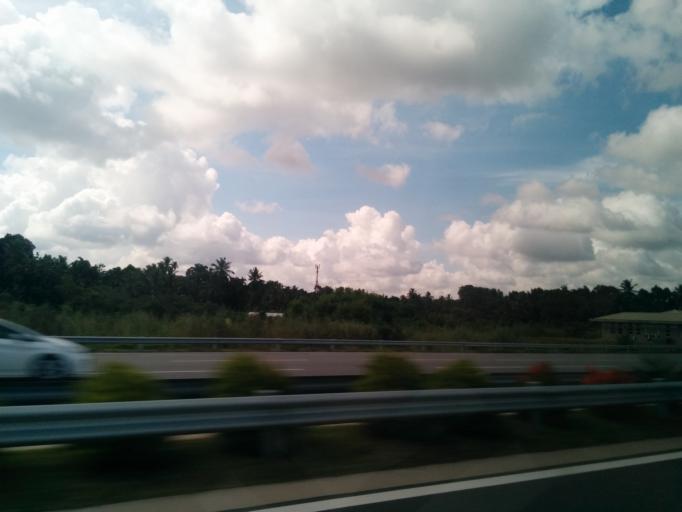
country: LK
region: Western
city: Hendala
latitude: 6.9957
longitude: 79.9040
